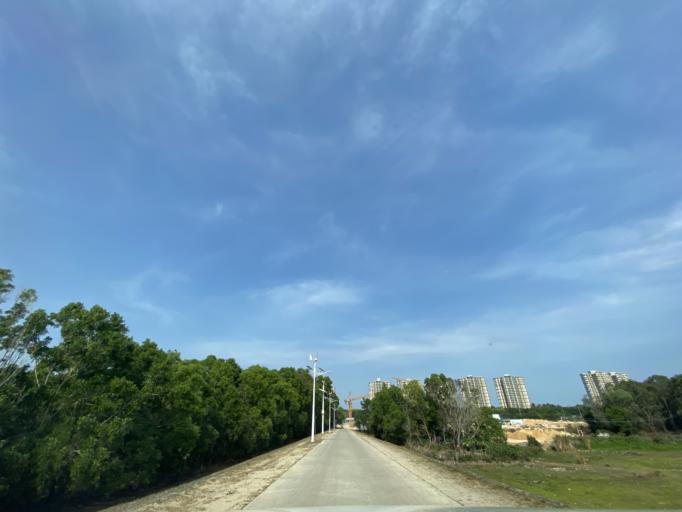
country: CN
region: Hainan
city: Yingzhou
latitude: 18.4080
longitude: 109.8346
